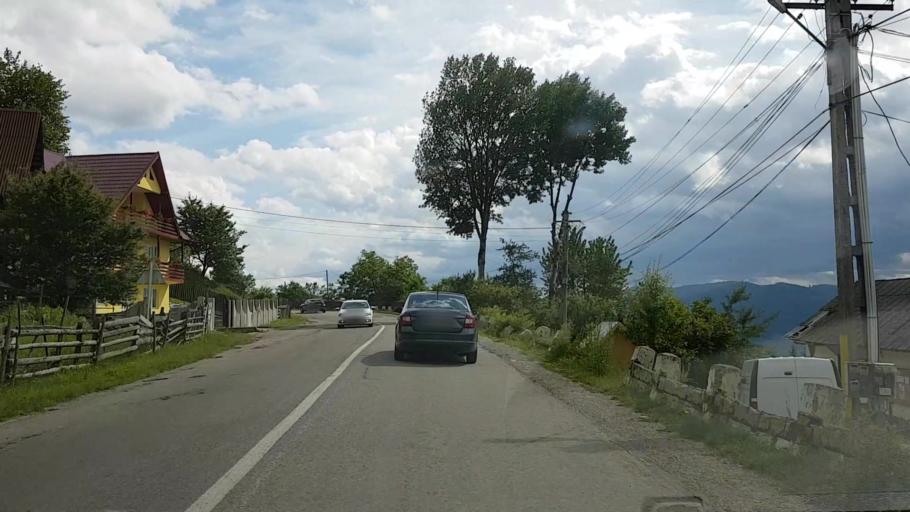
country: RO
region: Neamt
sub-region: Comuna Bicaz
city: Dodeni
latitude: 47.0026
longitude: 26.0976
